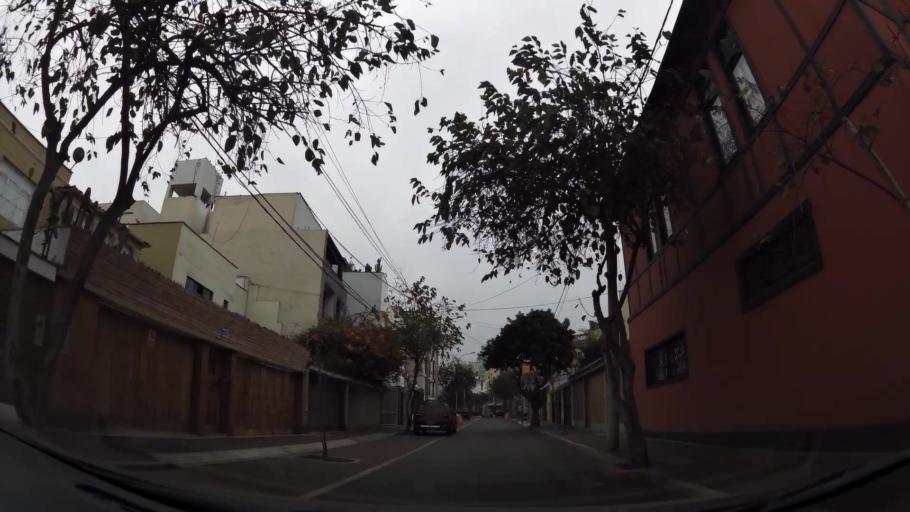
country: PE
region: Lima
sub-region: Lima
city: San Isidro
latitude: -12.1231
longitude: -77.0337
